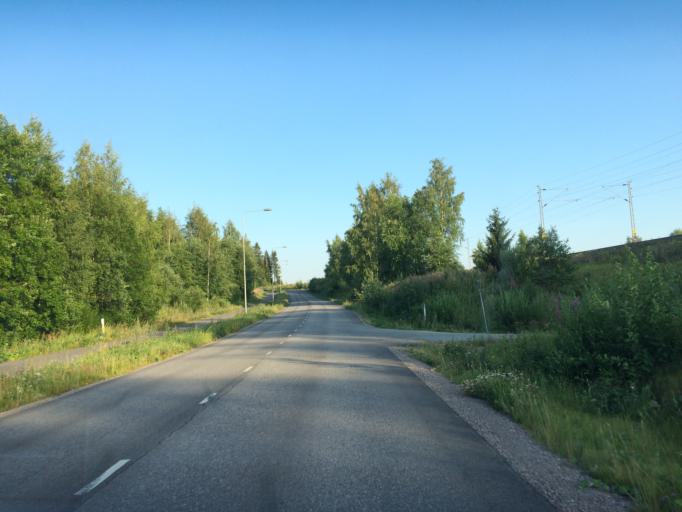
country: FI
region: Haeme
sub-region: Haemeenlinna
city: Parola
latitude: 61.0372
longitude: 24.3858
